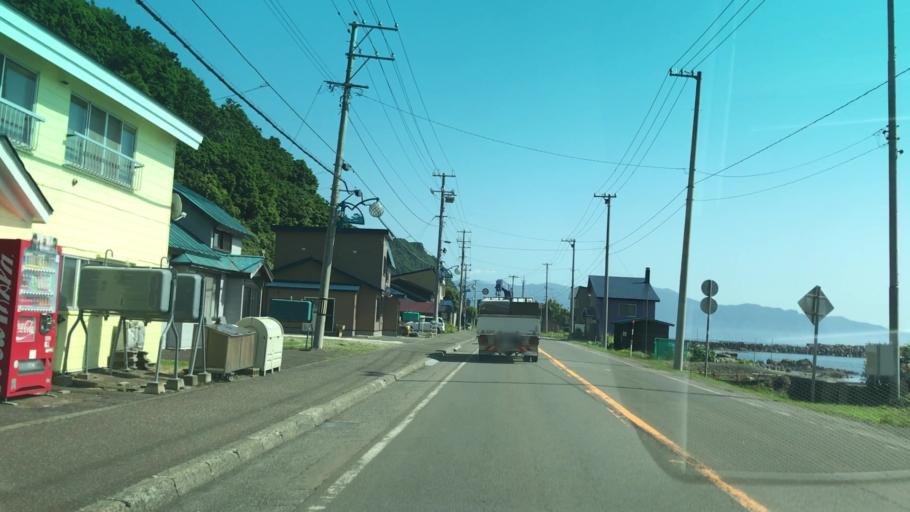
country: JP
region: Hokkaido
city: Iwanai
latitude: 43.1045
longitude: 140.4598
